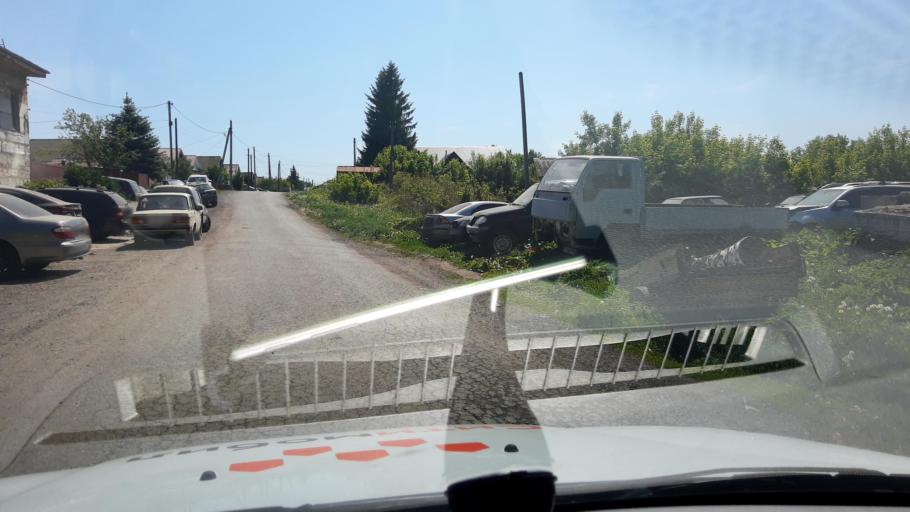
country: RU
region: Bashkortostan
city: Ufa
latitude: 54.5239
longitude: 55.9103
